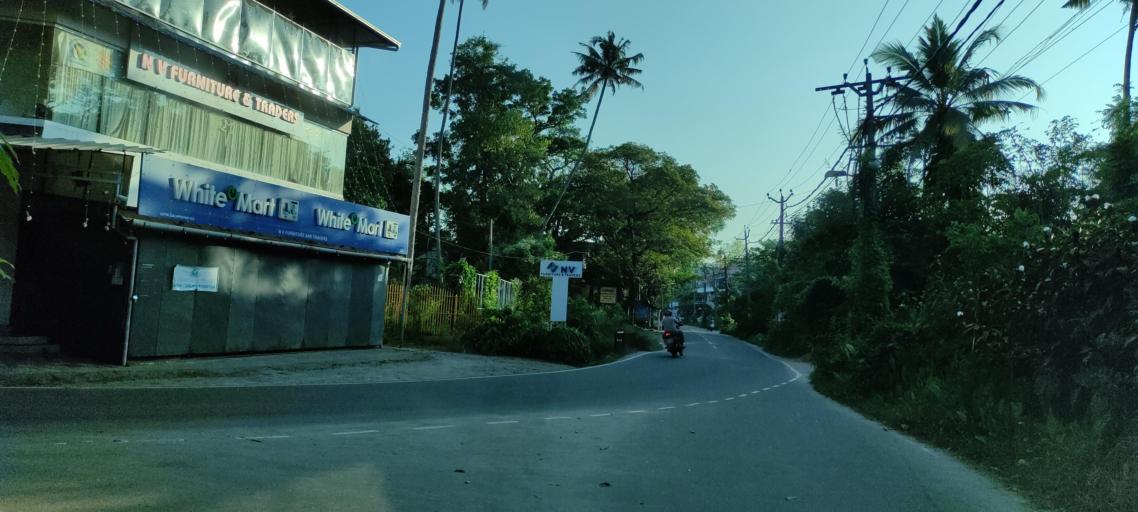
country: IN
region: Kerala
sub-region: Alappuzha
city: Vayalar
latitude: 9.6928
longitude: 76.3434
